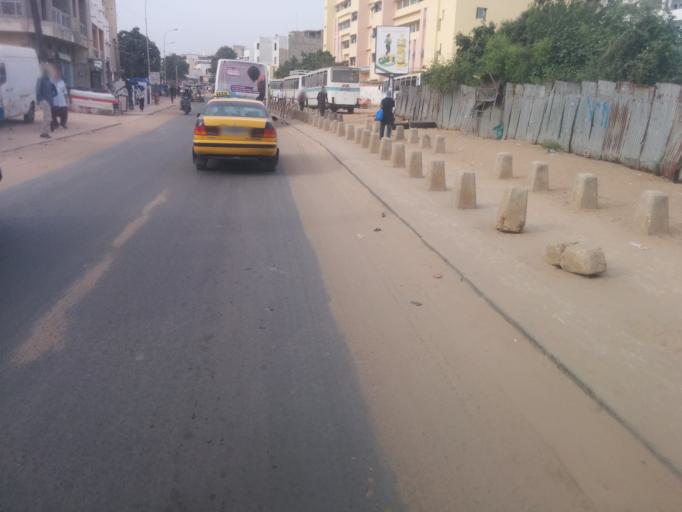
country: SN
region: Dakar
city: Grand Dakar
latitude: 14.7410
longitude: -17.4521
